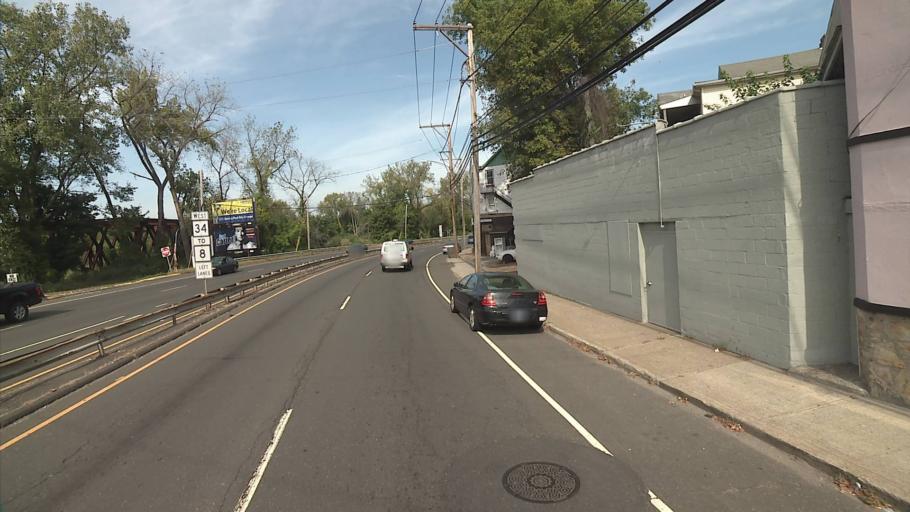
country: US
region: Connecticut
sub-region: New Haven County
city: Derby
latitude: 41.3156
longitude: -73.0802
